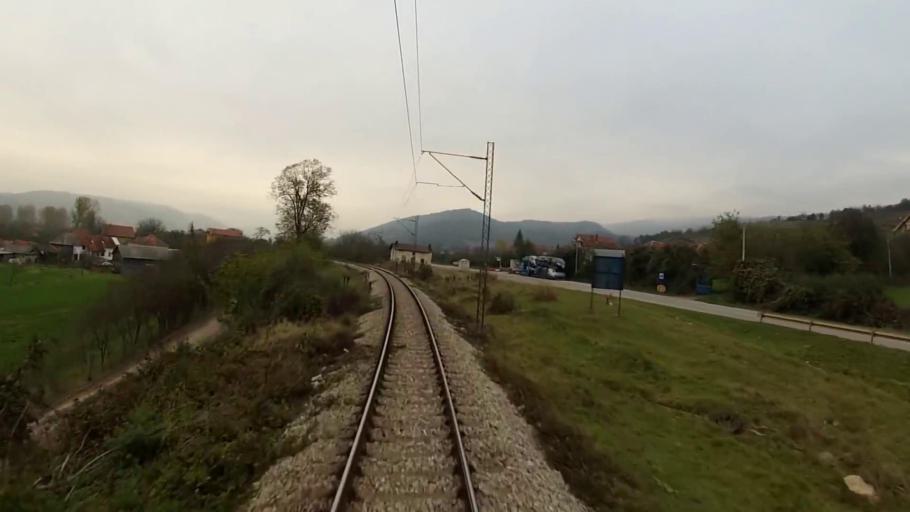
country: RS
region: Central Serbia
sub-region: Pirotski Okrug
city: Dimitrovgrad
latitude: 43.0050
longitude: 22.8085
